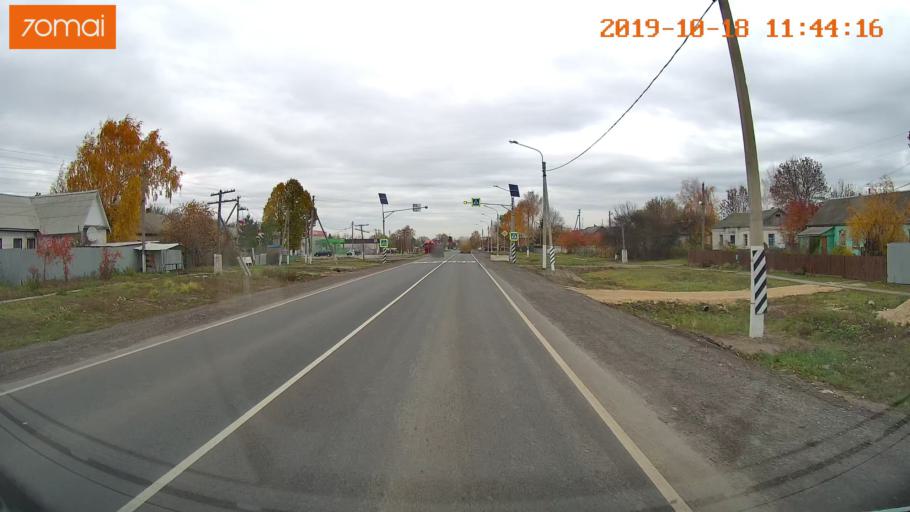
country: RU
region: Rjazan
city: Oktyabr'skiy
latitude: 54.2014
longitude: 38.9550
